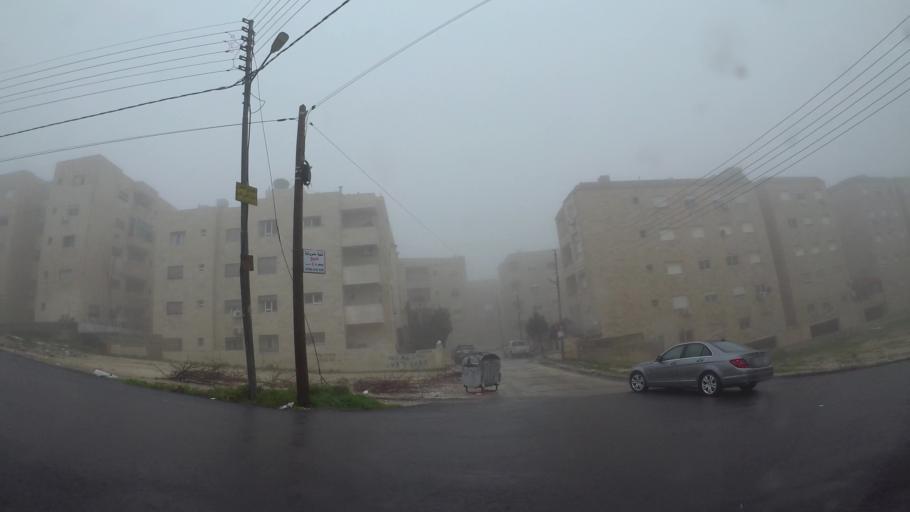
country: JO
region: Amman
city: Al Jubayhah
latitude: 32.0189
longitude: 35.8763
